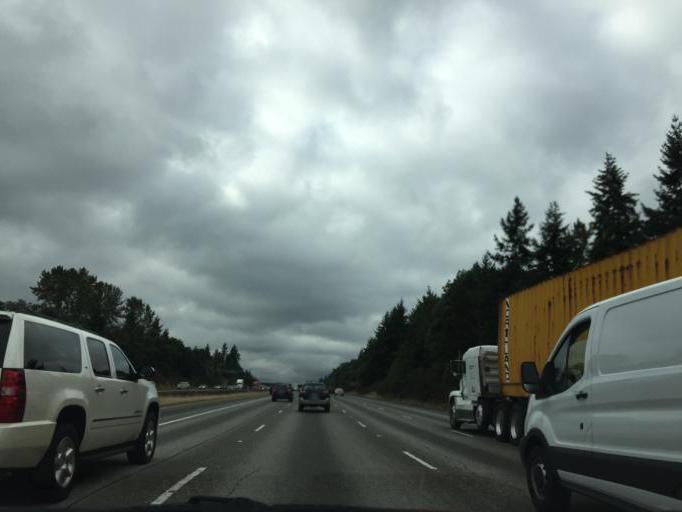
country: US
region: Washington
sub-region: King County
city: Des Moines
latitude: 47.4130
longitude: -122.2909
